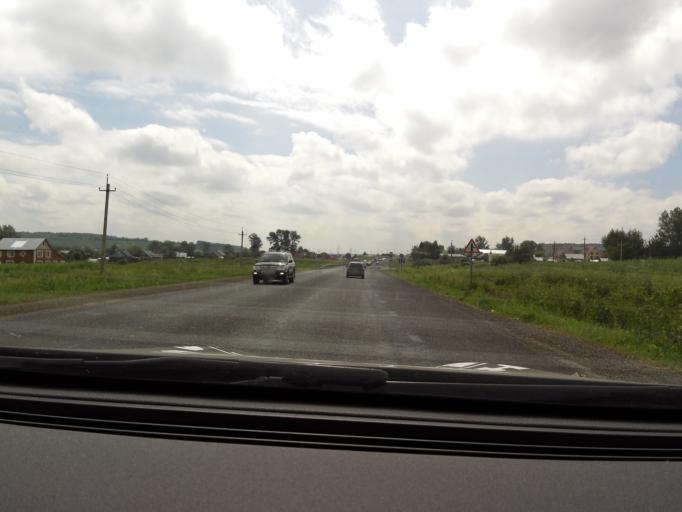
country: RU
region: Perm
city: Bershet'
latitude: 57.7365
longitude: 56.3737
